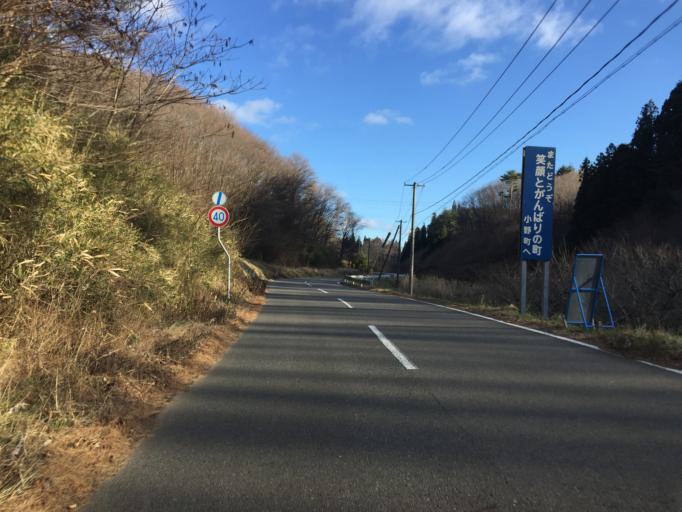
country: JP
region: Fukushima
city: Funehikimachi-funehiki
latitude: 37.2458
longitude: 140.6741
